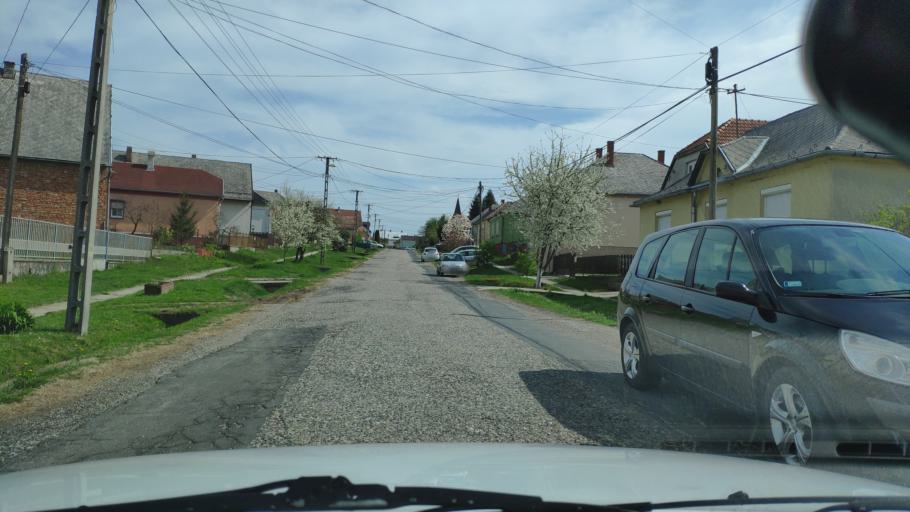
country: HU
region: Zala
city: Nagykanizsa
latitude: 46.4233
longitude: 17.0274
